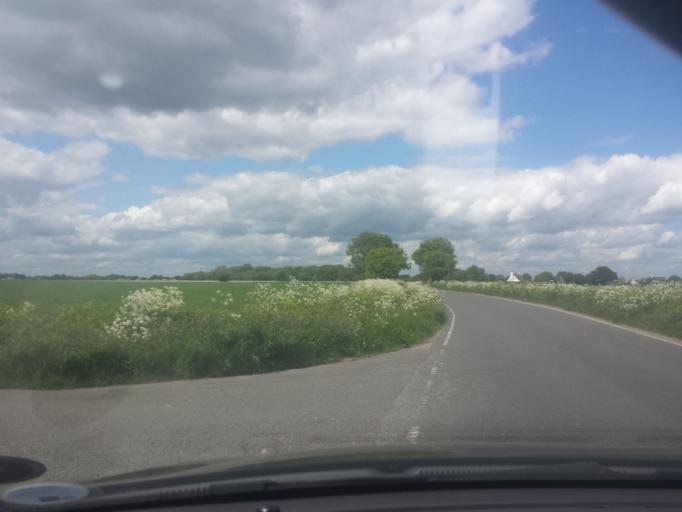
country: GB
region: England
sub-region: Essex
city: Little Clacton
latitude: 51.8912
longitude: 1.1498
